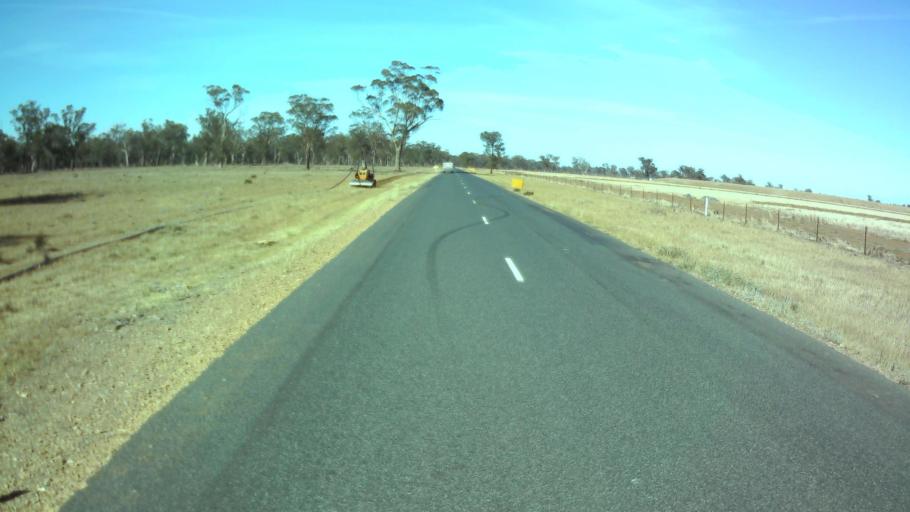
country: AU
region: New South Wales
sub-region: Weddin
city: Grenfell
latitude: -34.1270
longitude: 147.8015
